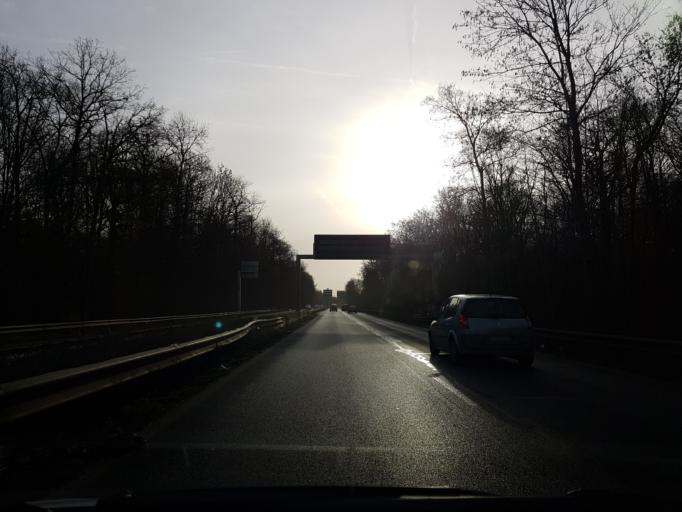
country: FR
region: Ile-de-France
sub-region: Departement de l'Essonne
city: Quincy-sous-Senart
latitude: 48.6524
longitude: 2.5276
